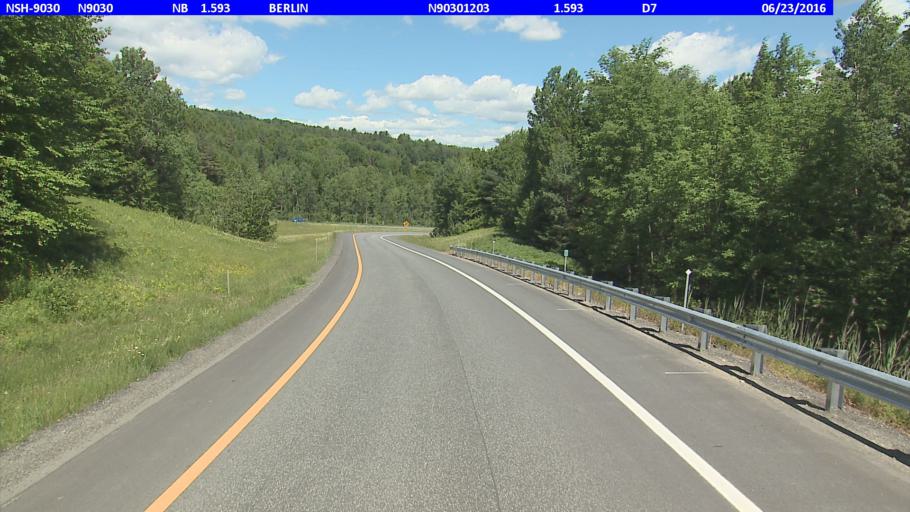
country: US
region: Vermont
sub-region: Washington County
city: Montpelier
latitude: 44.2233
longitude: -72.5562
